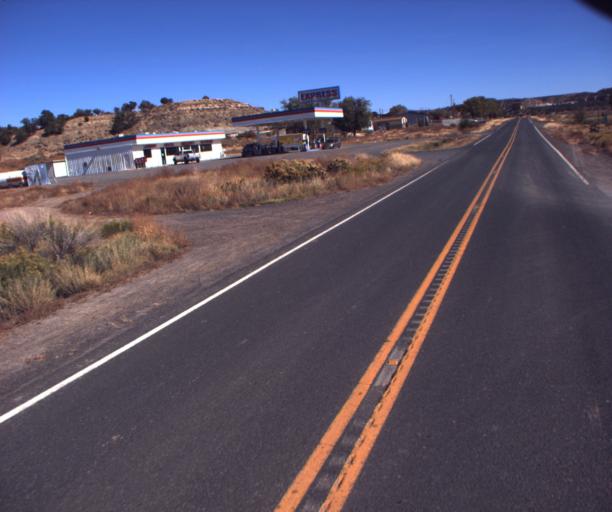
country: US
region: Arizona
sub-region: Apache County
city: Ganado
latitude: 35.7466
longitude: -109.8604
